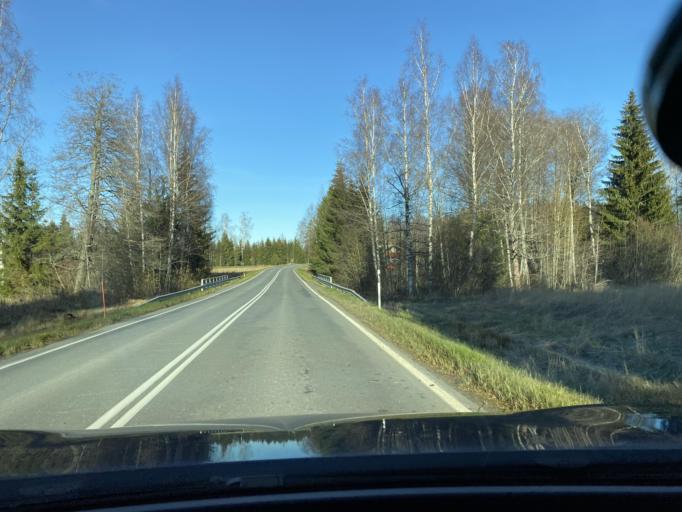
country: FI
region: Haeme
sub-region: Forssa
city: Tammela
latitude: 60.8458
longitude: 23.8371
